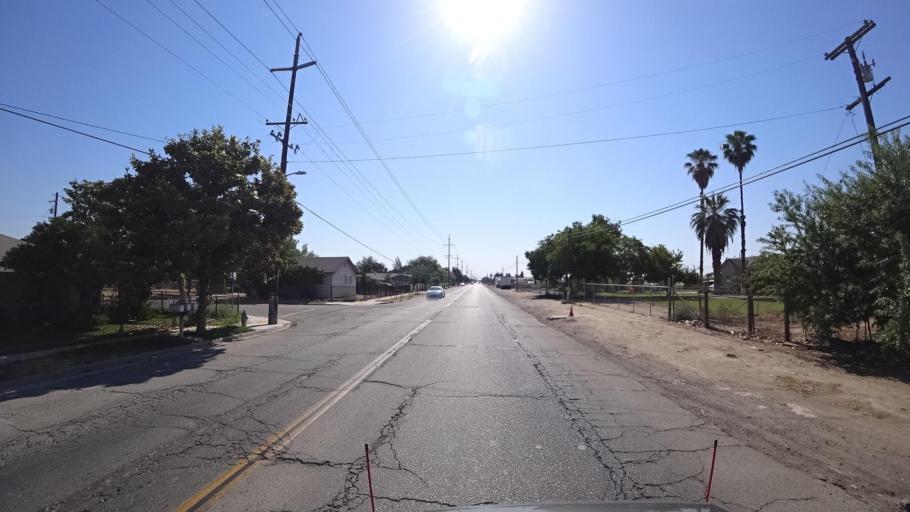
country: US
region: California
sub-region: Fresno County
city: West Park
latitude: 36.7069
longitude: -119.8138
